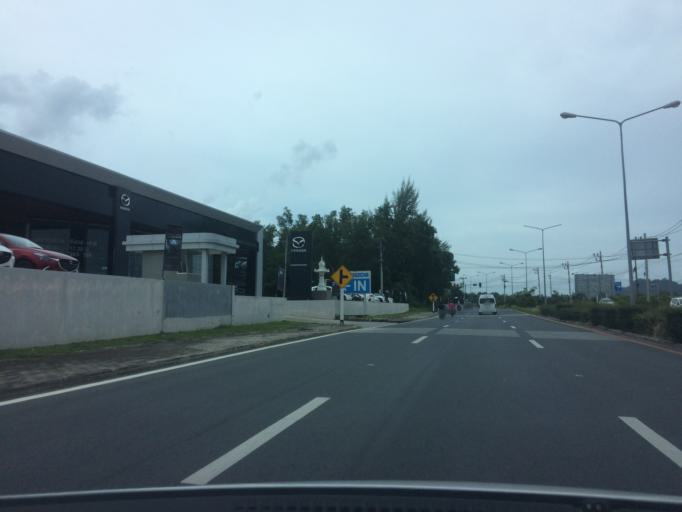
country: TH
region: Phuket
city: Mueang Phuket
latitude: 7.8704
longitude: 98.3566
